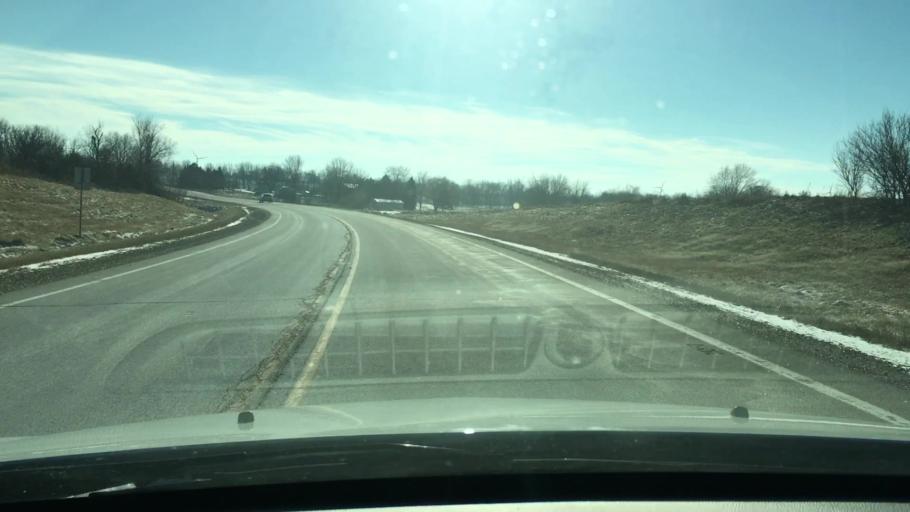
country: US
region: Illinois
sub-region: LaSalle County
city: Mendota
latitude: 41.7109
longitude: -89.0911
